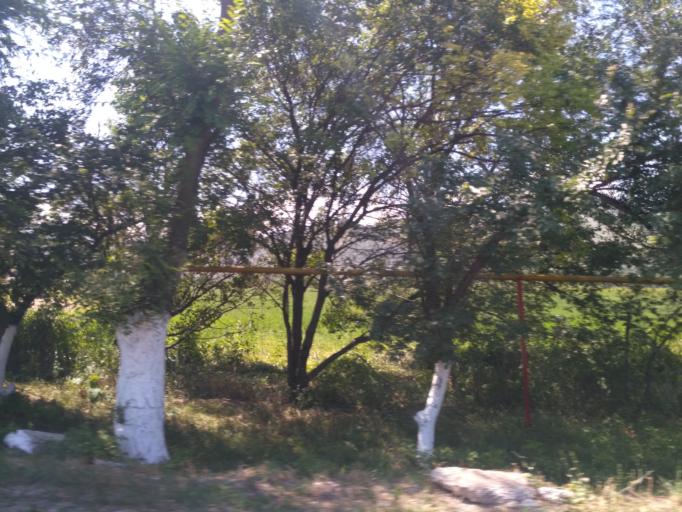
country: KZ
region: Almaty Oblysy
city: Burunday
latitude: 43.1665
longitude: 76.5950
